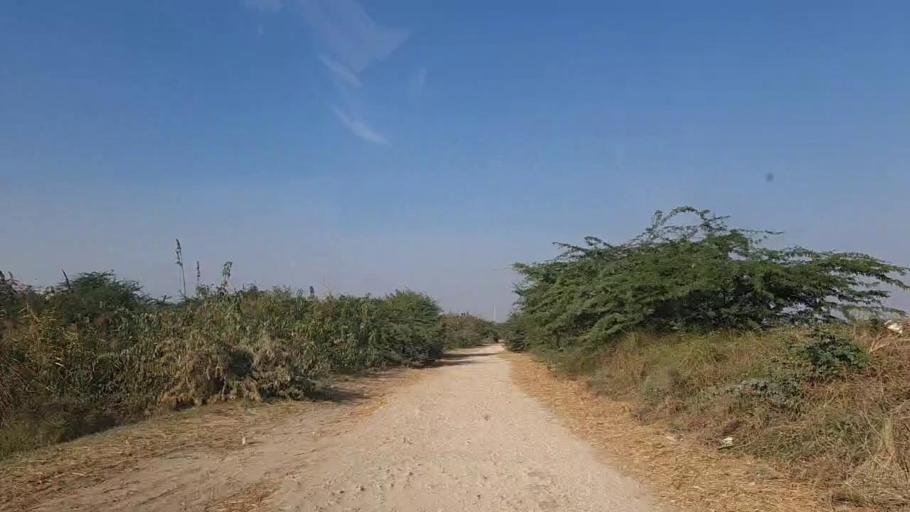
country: PK
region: Sindh
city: Thatta
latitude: 24.7492
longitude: 67.9599
